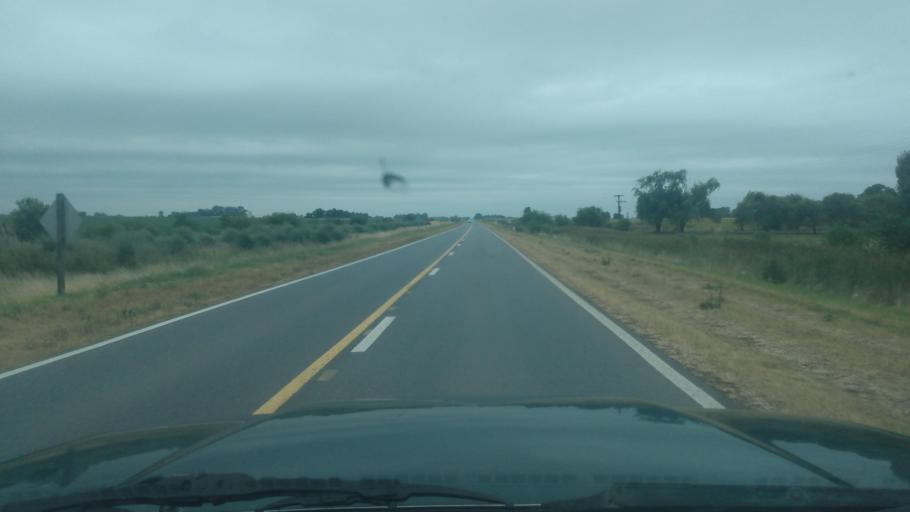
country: AR
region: Buenos Aires
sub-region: Partido de Bragado
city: Bragado
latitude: -35.3218
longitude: -60.6389
